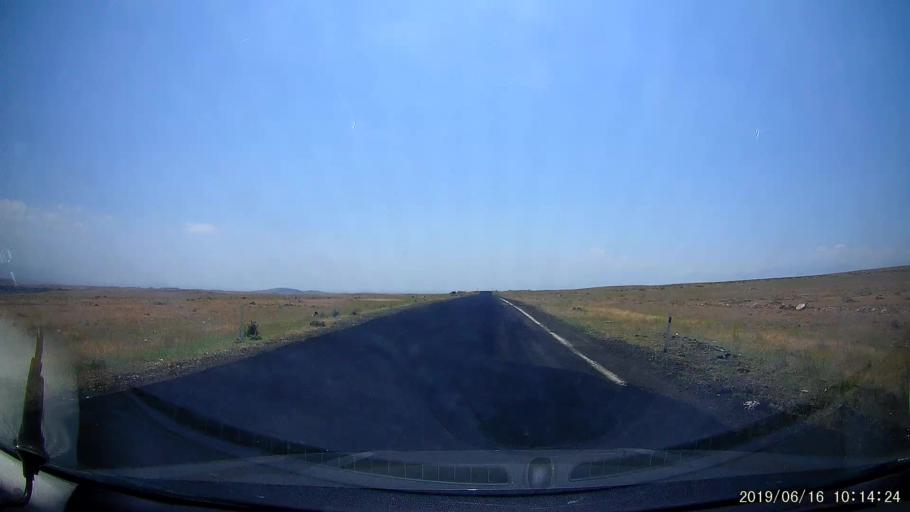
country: TR
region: Igdir
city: Tuzluca
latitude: 40.1851
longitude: 43.6622
